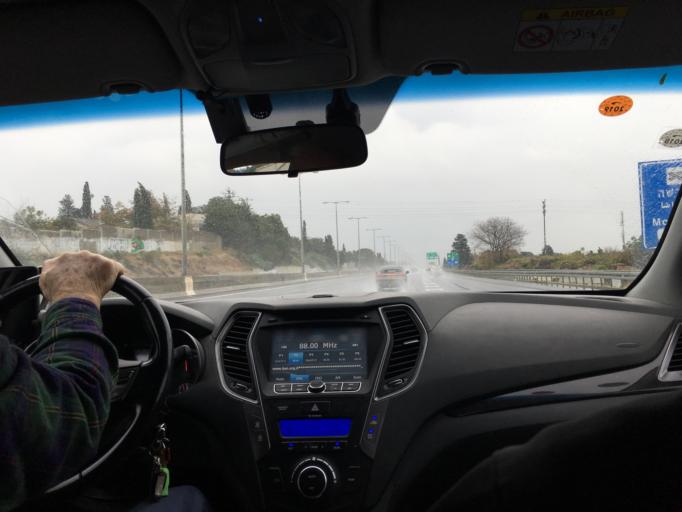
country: IL
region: Tel Aviv
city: Ramat HaSharon
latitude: 32.1307
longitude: 34.8411
